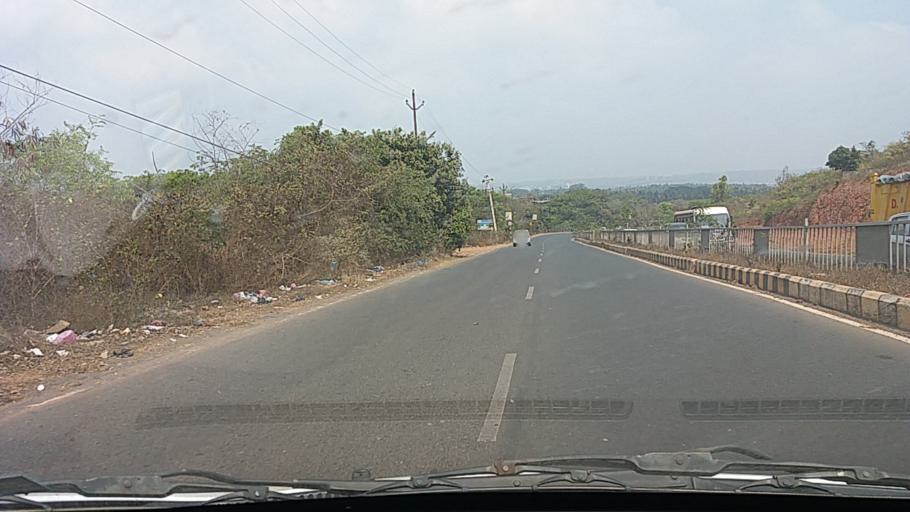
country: IN
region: Goa
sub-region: North Goa
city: Bambolim
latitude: 15.4659
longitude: 73.8518
